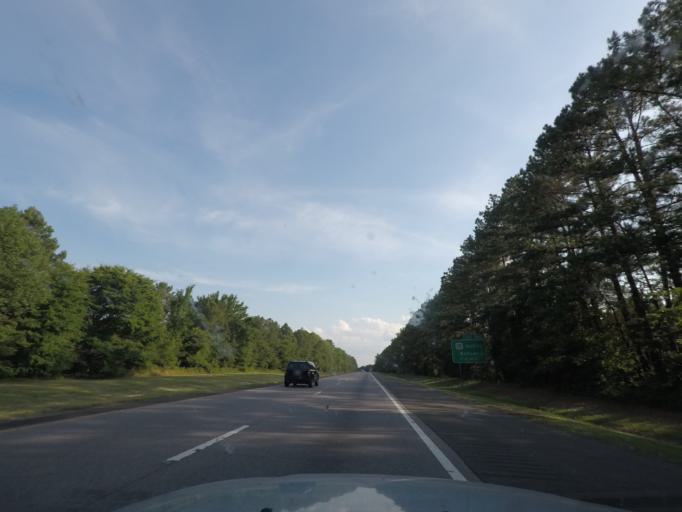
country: US
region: North Carolina
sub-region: Granville County
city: Butner
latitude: 36.1038
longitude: -78.7551
